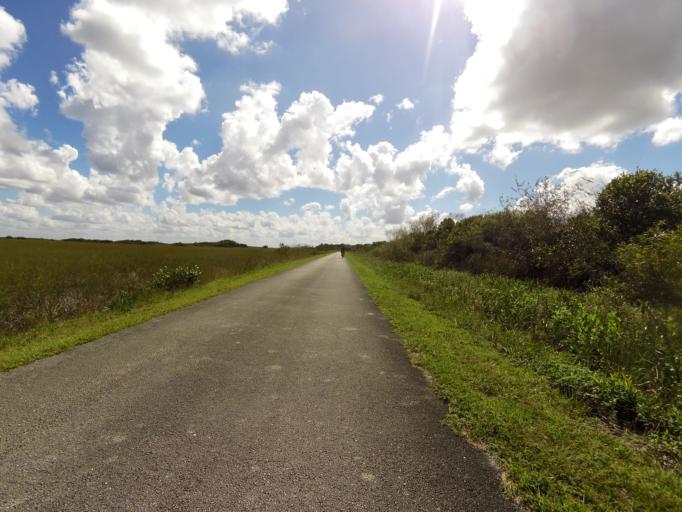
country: US
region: Florida
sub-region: Miami-Dade County
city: The Hammocks
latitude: 25.7303
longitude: -80.7667
